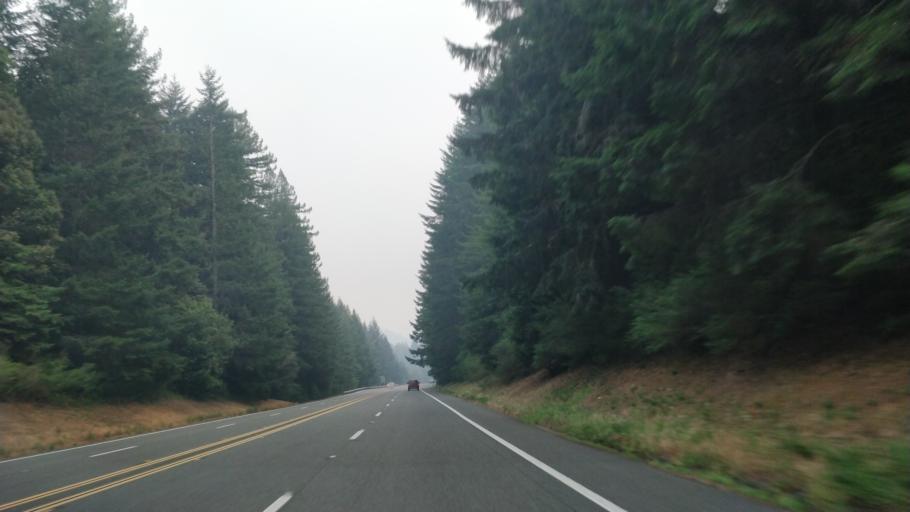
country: US
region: California
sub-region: Humboldt County
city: Rio Dell
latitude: 40.3887
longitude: -123.9316
